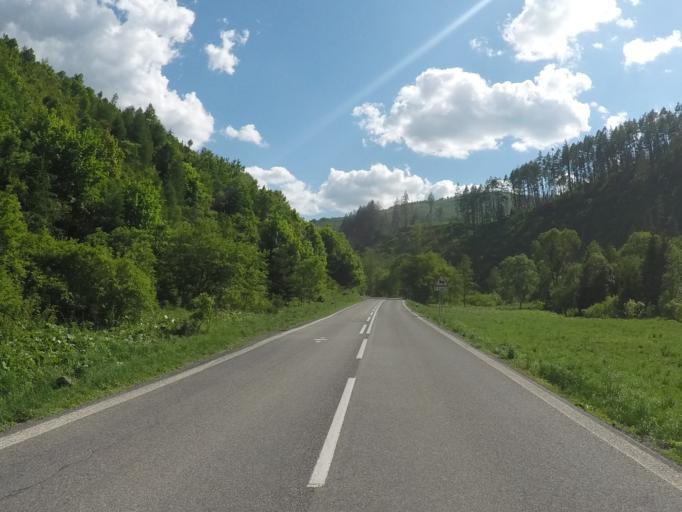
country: SK
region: Presovsky
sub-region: Okres Poprad
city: Poprad
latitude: 48.9699
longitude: 20.2953
